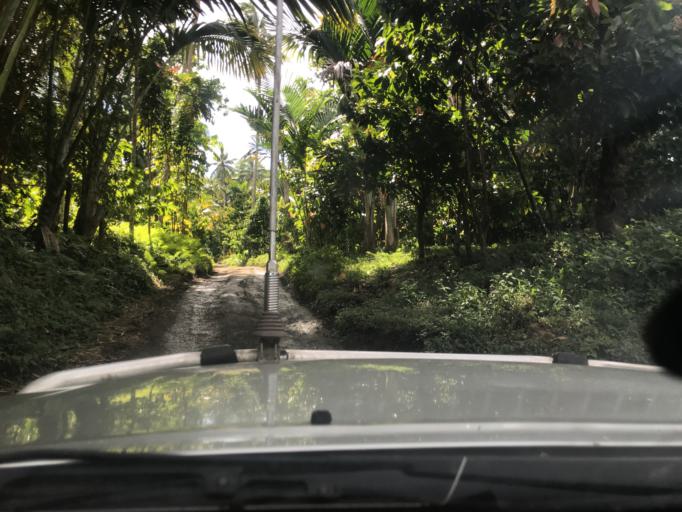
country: SB
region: Malaita
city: Auki
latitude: -8.9330
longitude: 160.7677
